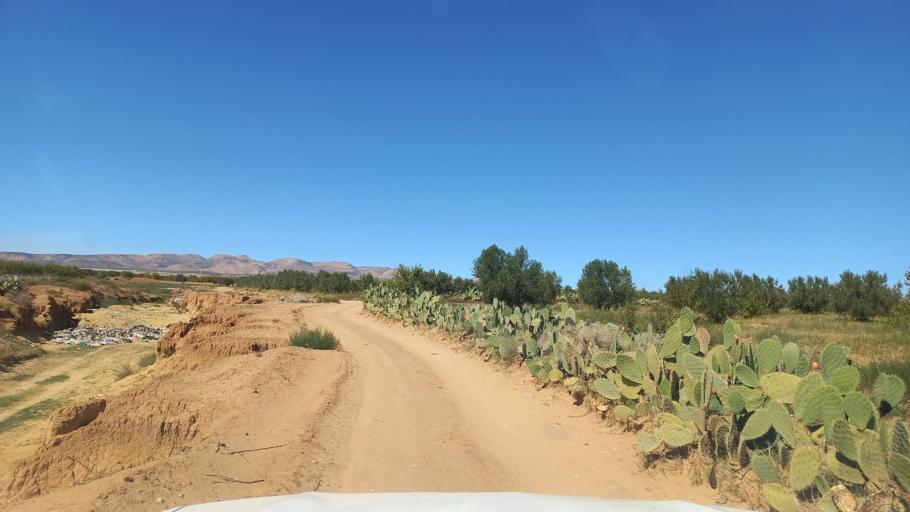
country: TN
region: Al Qasrayn
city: Sbiba
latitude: 35.3604
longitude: 9.0847
